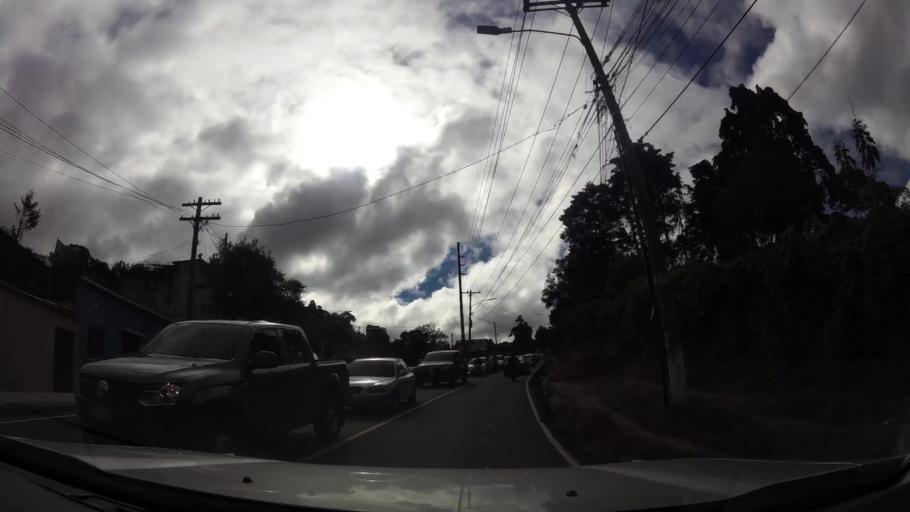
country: GT
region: Guatemala
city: Santa Catarina Pinula
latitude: 14.5745
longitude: -90.4896
